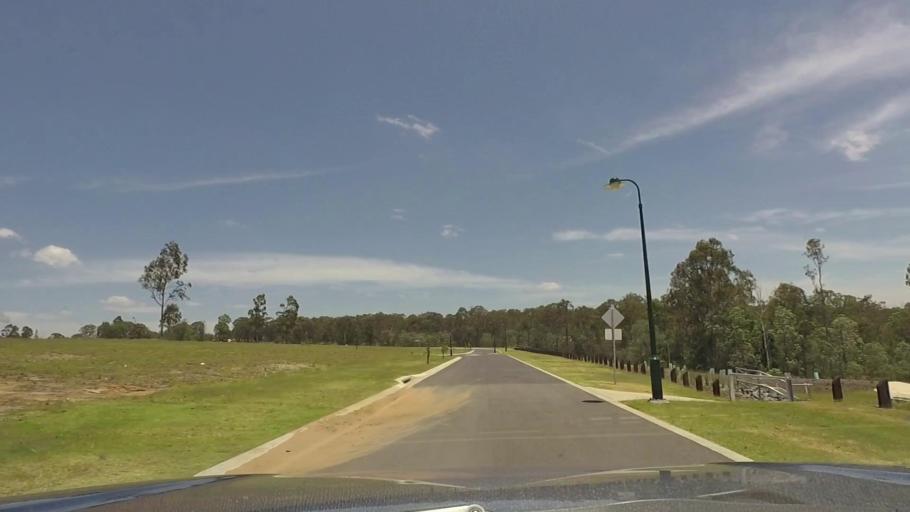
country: AU
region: Queensland
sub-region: Logan
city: Chambers Flat
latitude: -27.7718
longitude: 153.0867
